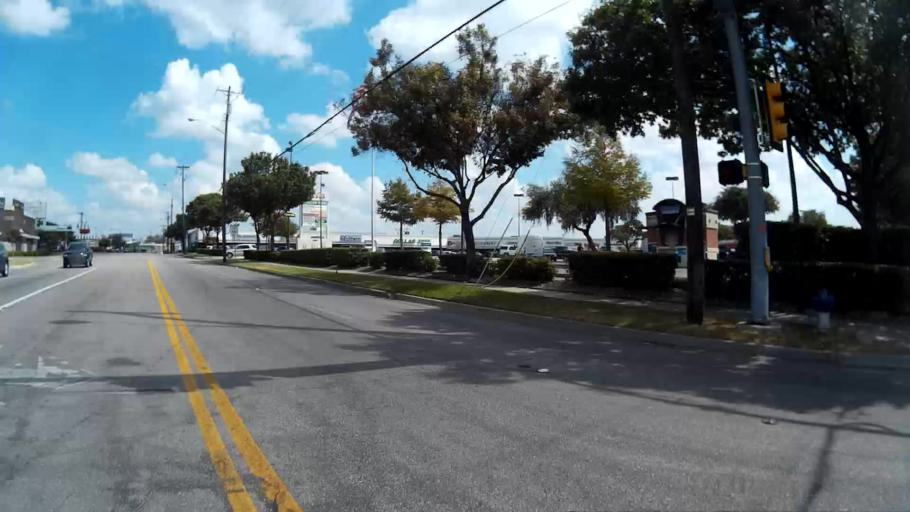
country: US
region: Texas
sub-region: Dallas County
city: Highland Park
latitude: 32.8095
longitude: -96.7723
